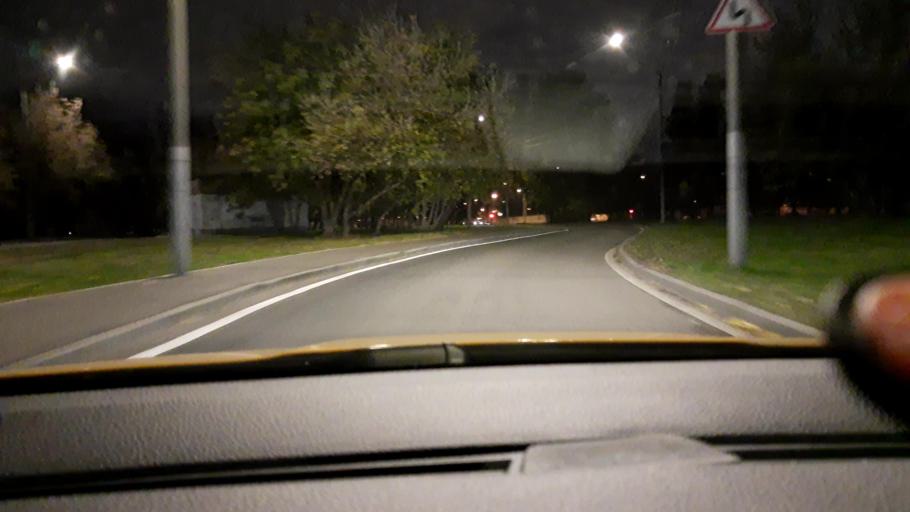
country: RU
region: Moscow
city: Kuz'minki
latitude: 55.6758
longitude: 37.8006
